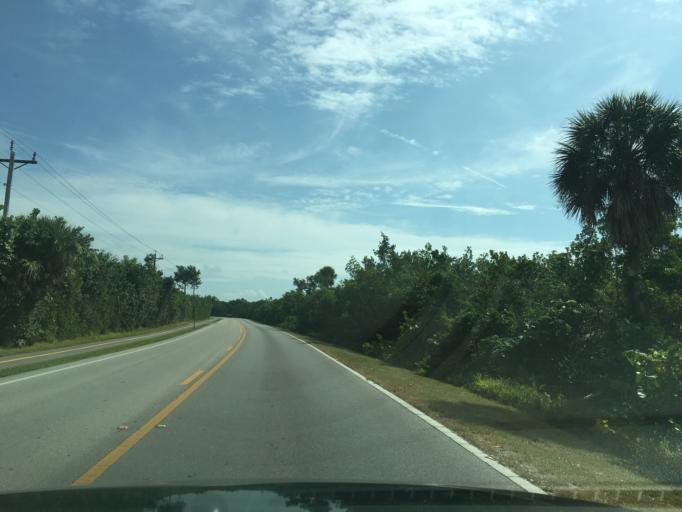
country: US
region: Florida
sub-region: Lee County
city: Saint James City
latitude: 26.4713
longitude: -82.1635
